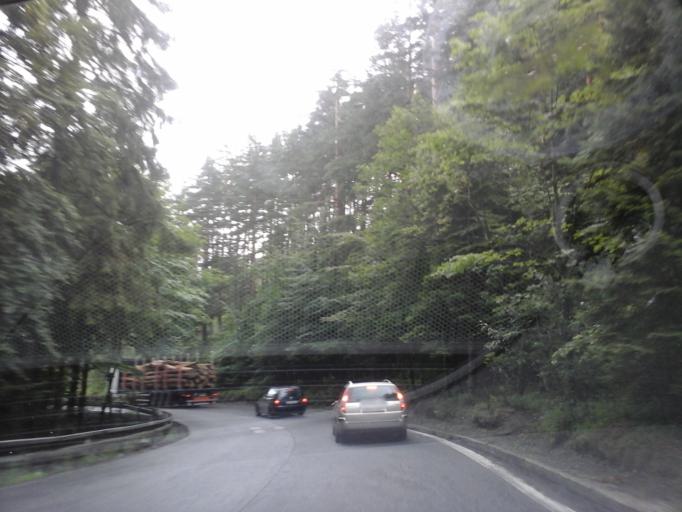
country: SK
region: Kosicky
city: Dobsina
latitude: 48.9069
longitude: 20.2568
